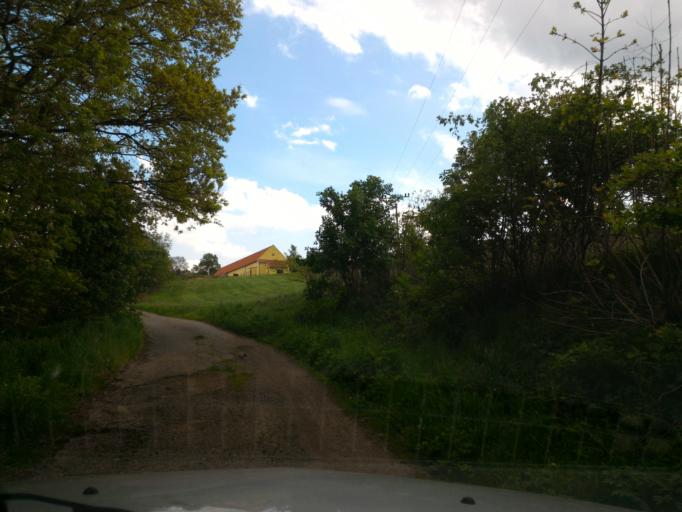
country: CZ
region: Vysocina
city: Ledec nad Sazavou
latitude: 49.6535
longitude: 15.2916
